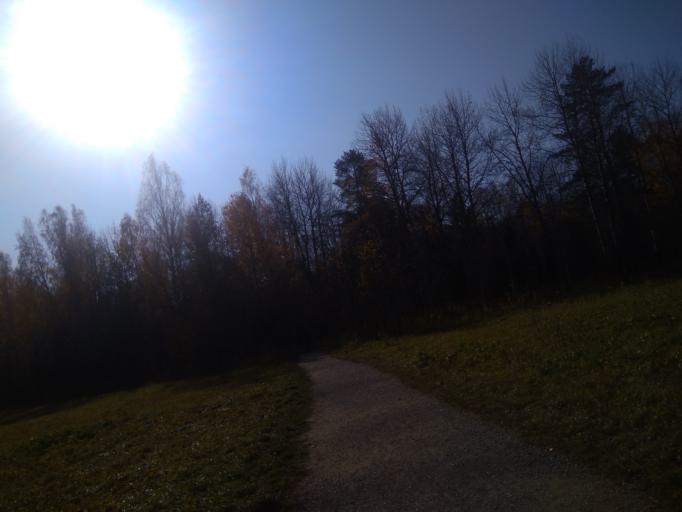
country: RU
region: Sverdlovsk
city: Mikhaylovsk
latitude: 56.5220
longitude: 59.2349
